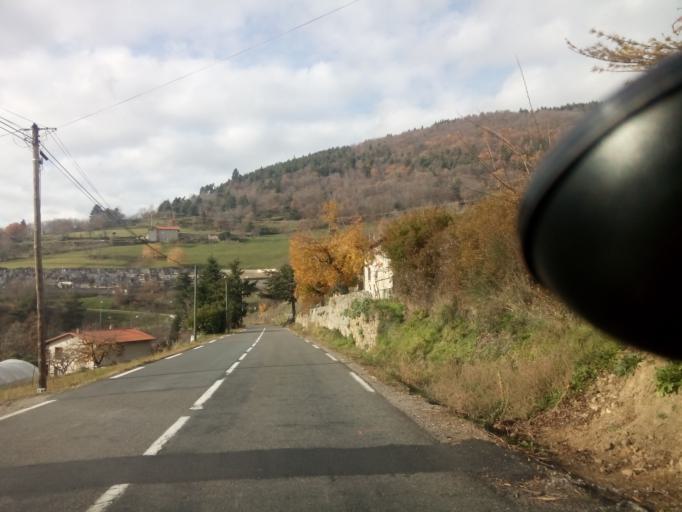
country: FR
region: Rhone-Alpes
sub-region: Departement de la Loire
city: Bourg-Argental
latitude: 45.3010
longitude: 4.5710
